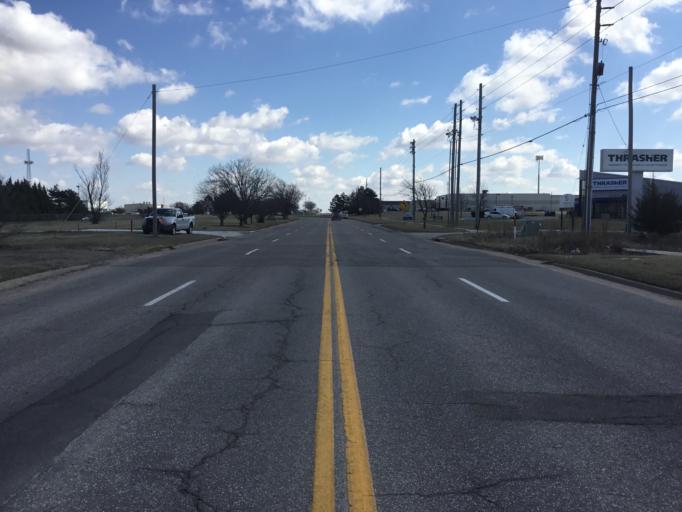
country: US
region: Kansas
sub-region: Sedgwick County
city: Bellaire
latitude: 37.7522
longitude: -97.2360
